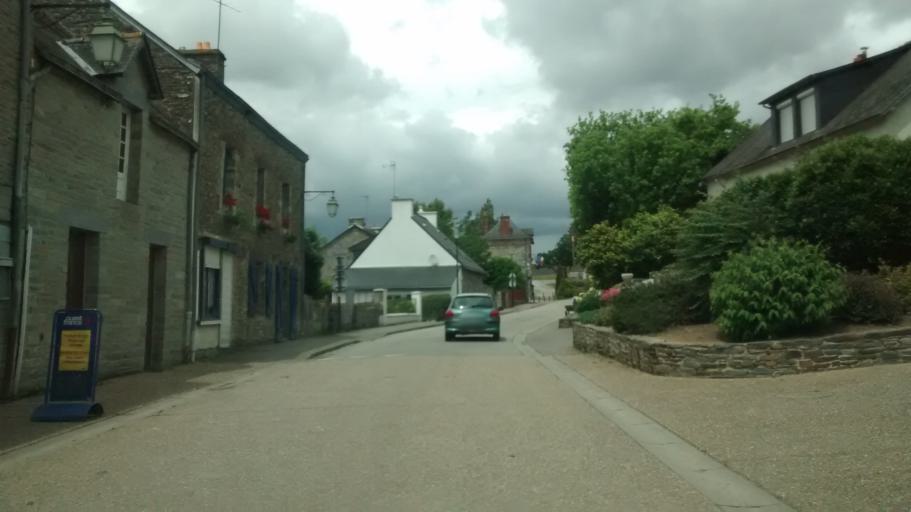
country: FR
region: Brittany
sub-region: Departement d'Ille-et-Vilaine
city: Sixt-sur-Aff
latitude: 47.7841
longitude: -2.1065
